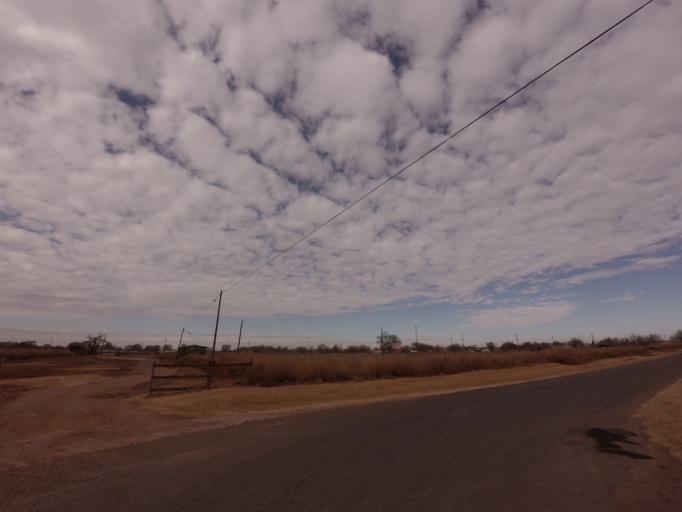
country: US
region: New Mexico
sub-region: Curry County
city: Clovis
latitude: 34.3956
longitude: -103.2266
